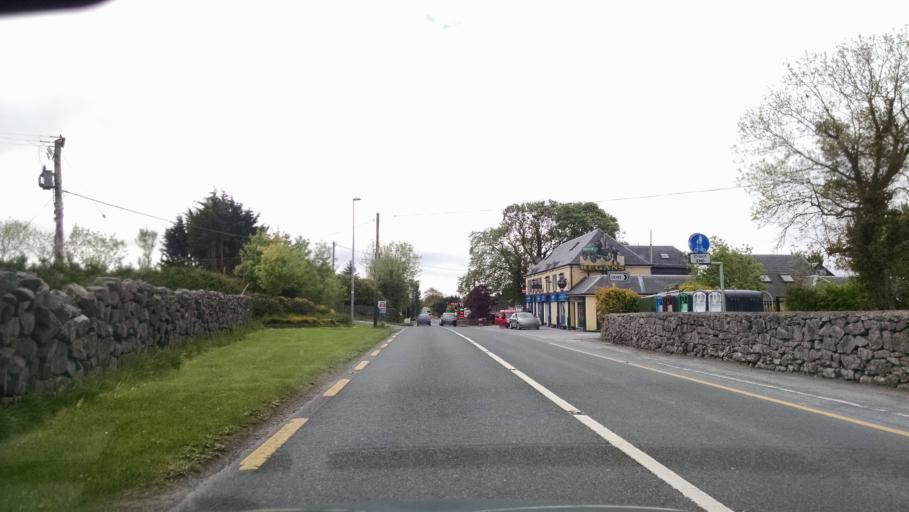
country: IE
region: Connaught
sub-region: County Galway
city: Claregalway
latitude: 53.3760
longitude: -9.0161
